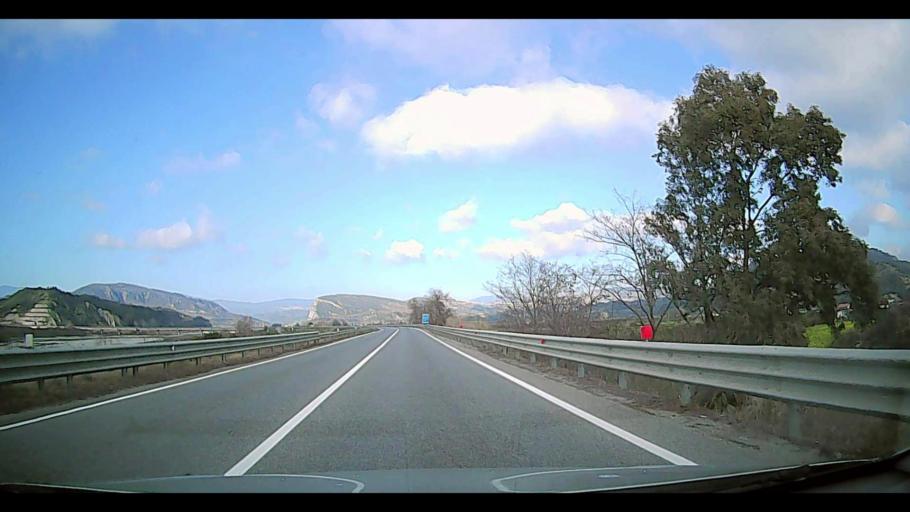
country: IT
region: Calabria
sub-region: Provincia di Crotone
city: Santa Severina
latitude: 39.1738
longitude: 16.9392
